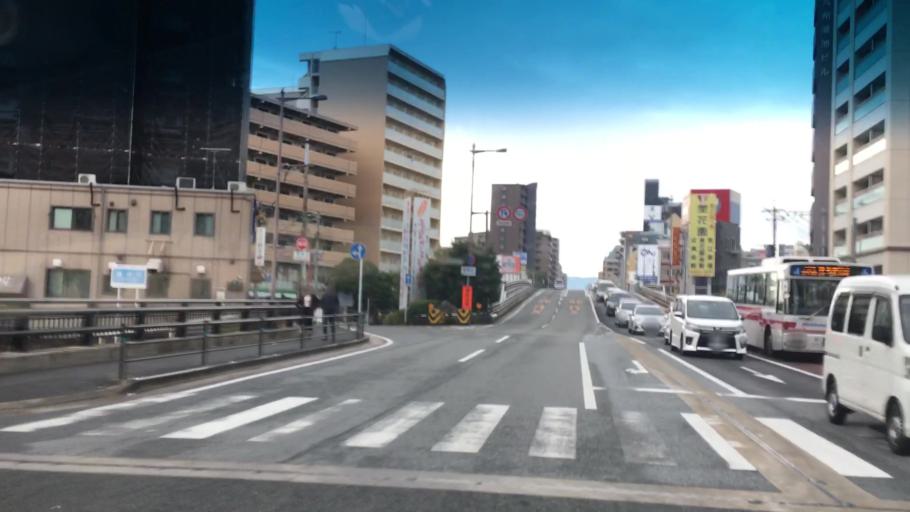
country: JP
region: Fukuoka
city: Fukuoka-shi
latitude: 33.5763
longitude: 130.3745
